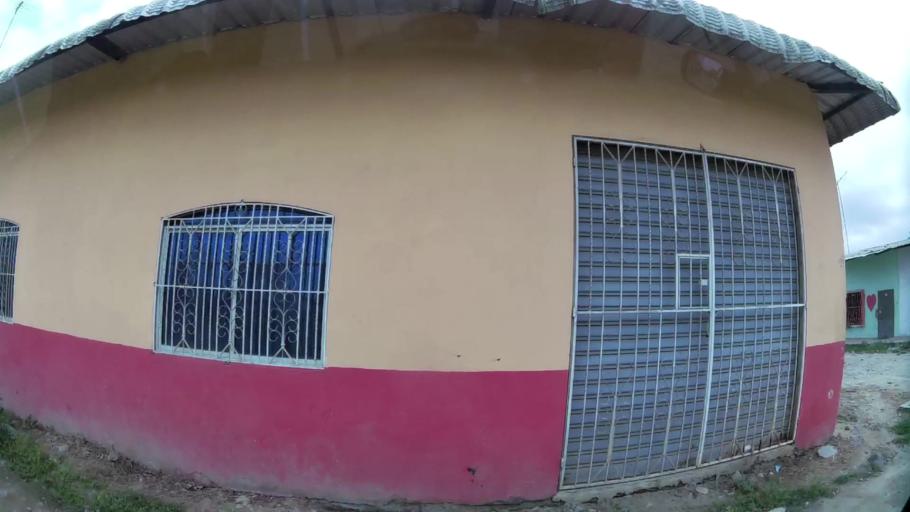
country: EC
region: Guayas
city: Naranjal
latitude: -2.6781
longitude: -79.6272
